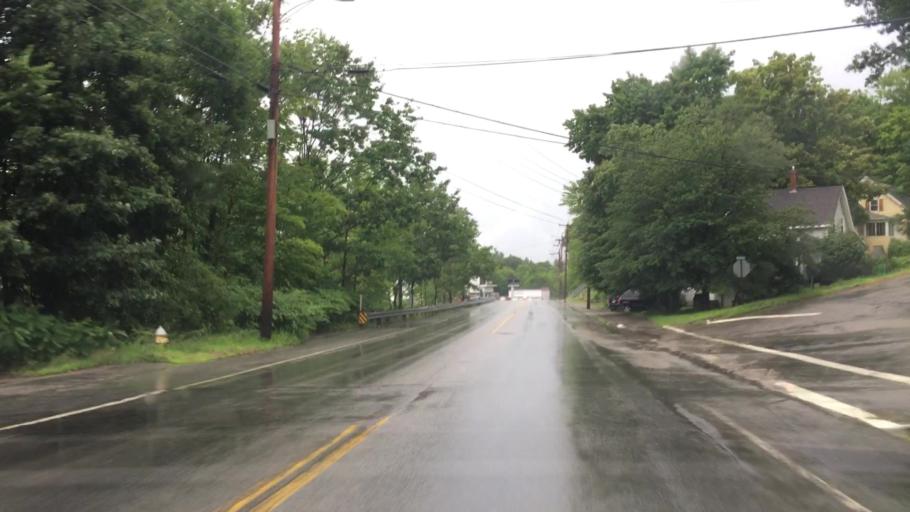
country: US
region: Maine
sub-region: Kennebec County
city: Gardiner
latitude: 44.2233
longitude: -69.7842
